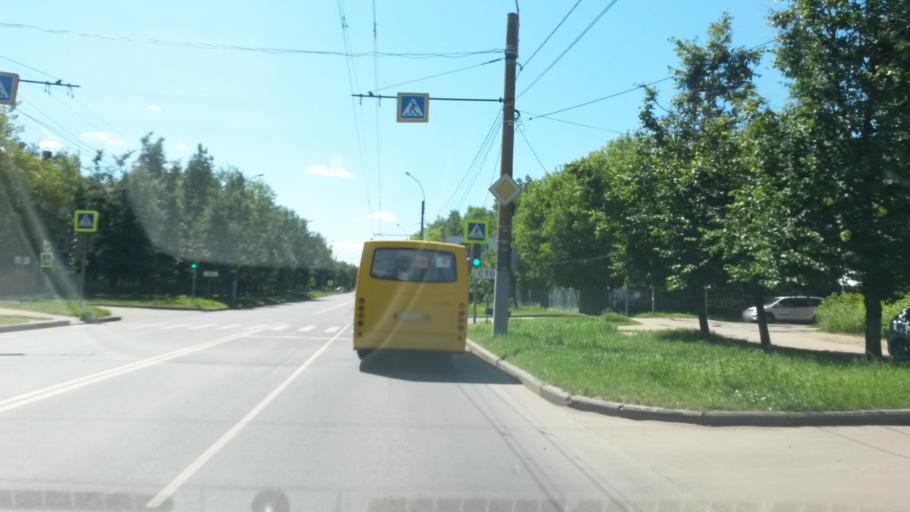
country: RU
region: Ivanovo
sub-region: Gorod Ivanovo
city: Ivanovo
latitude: 56.9808
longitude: 40.9673
